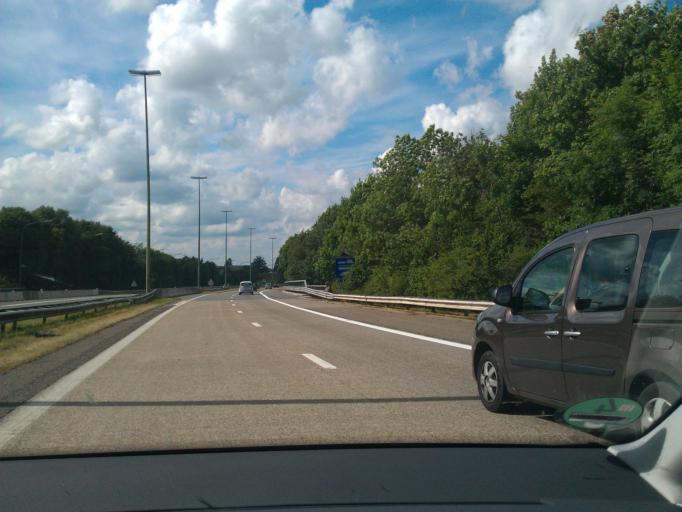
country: BE
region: Wallonia
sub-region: Province de Liege
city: Verviers
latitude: 50.5559
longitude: 5.8605
